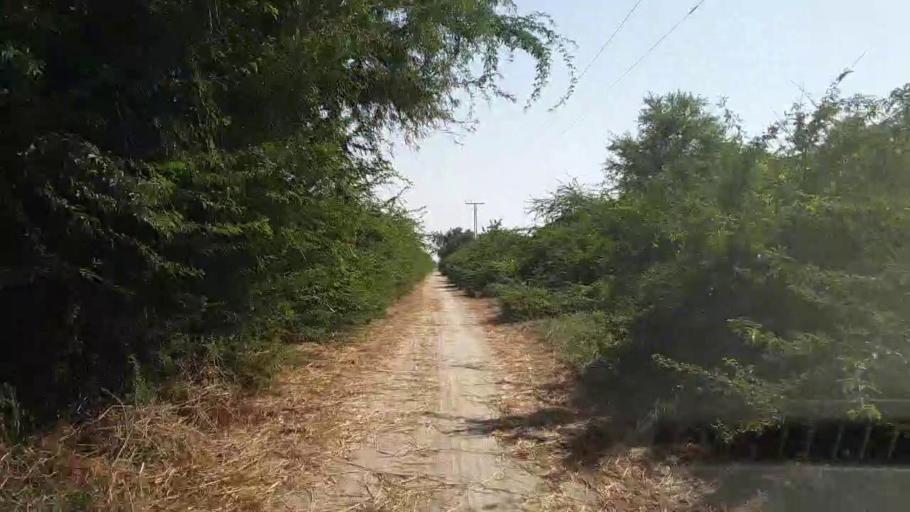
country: PK
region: Sindh
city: Tando Bago
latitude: 24.6420
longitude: 68.9887
